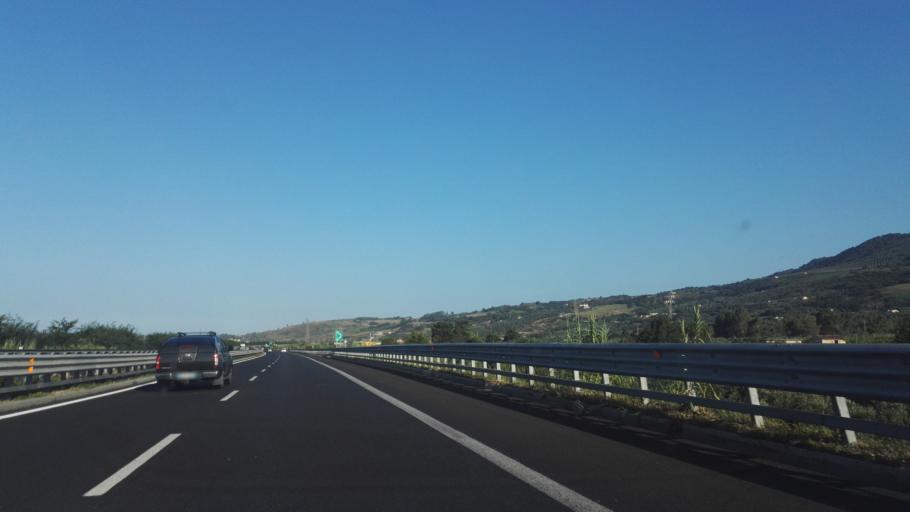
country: IT
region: Calabria
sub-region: Provincia di Catanzaro
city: Gizzeria
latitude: 38.9398
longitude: 16.2040
